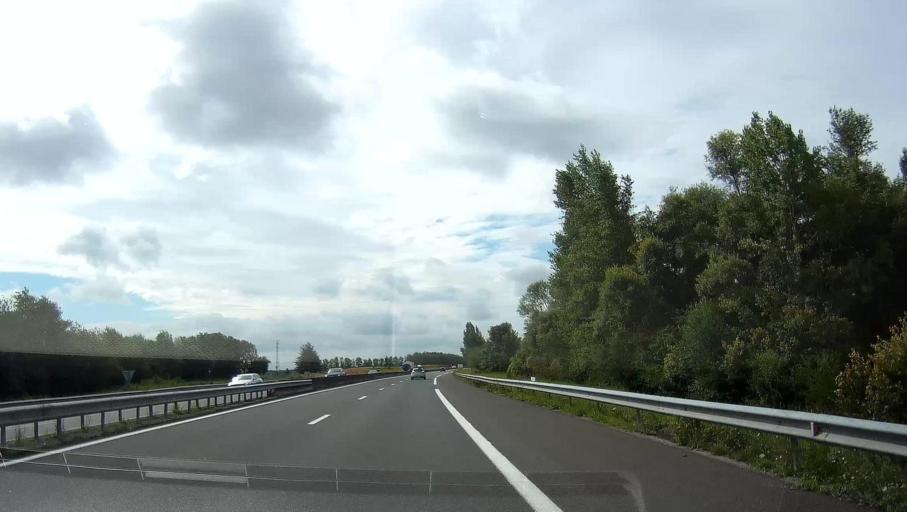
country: FR
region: Champagne-Ardenne
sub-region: Departement de la Marne
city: Fagnieres
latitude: 49.0103
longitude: 4.2976
